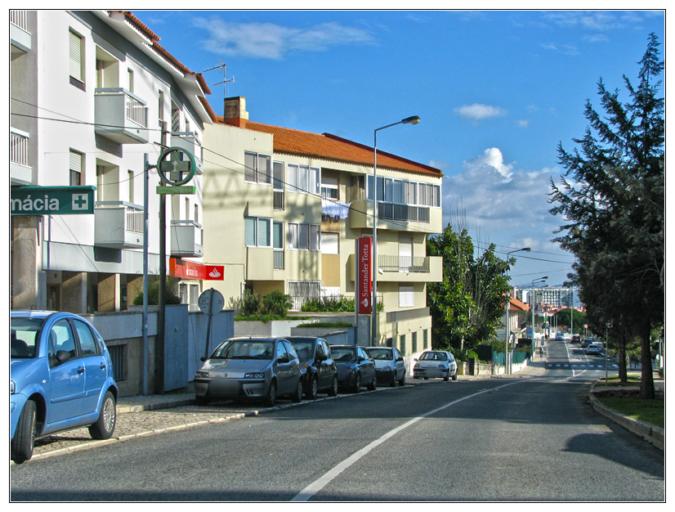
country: PT
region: Lisbon
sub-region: Cascais
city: Sao Domingos de Rana
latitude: 38.7014
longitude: -9.3401
